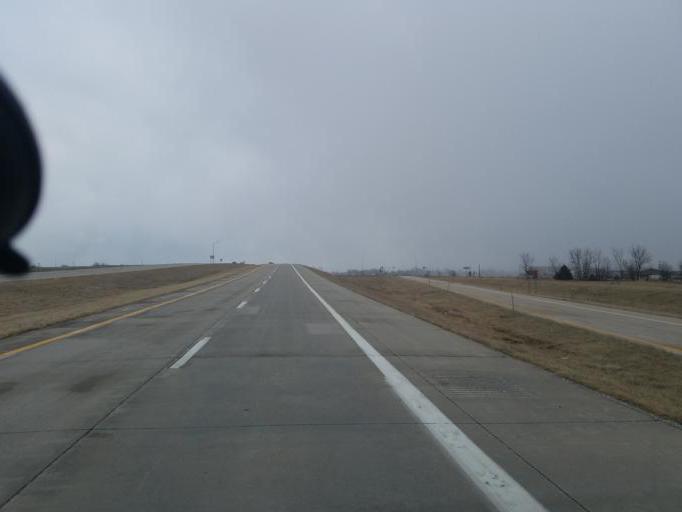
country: US
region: Missouri
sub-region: Randolph County
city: Moberly
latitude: 39.4473
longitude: -92.4268
